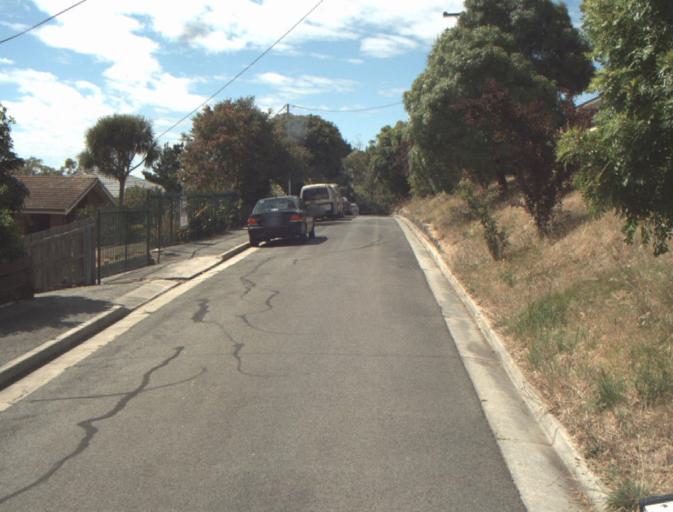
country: AU
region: Tasmania
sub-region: Launceston
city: West Launceston
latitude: -41.4542
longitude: 147.1280
